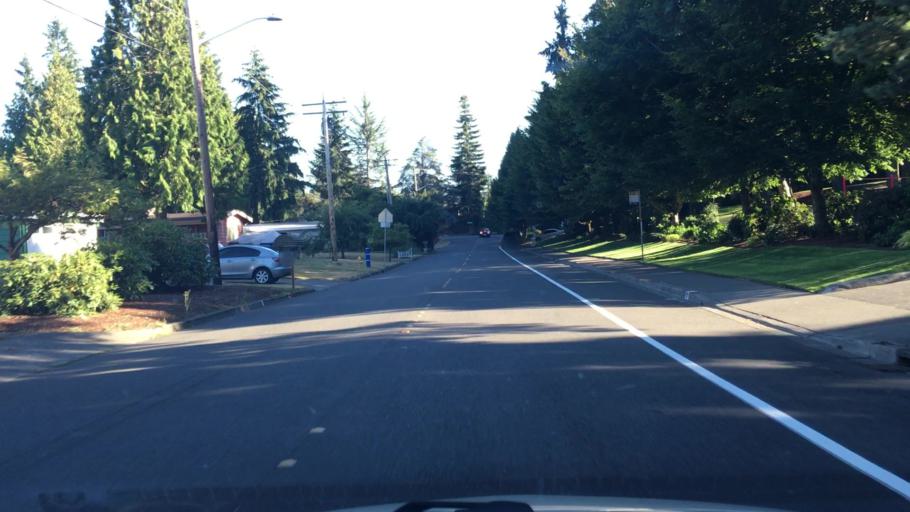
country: US
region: Washington
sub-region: King County
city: West Lake Sammamish
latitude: 47.5995
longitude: -122.1210
